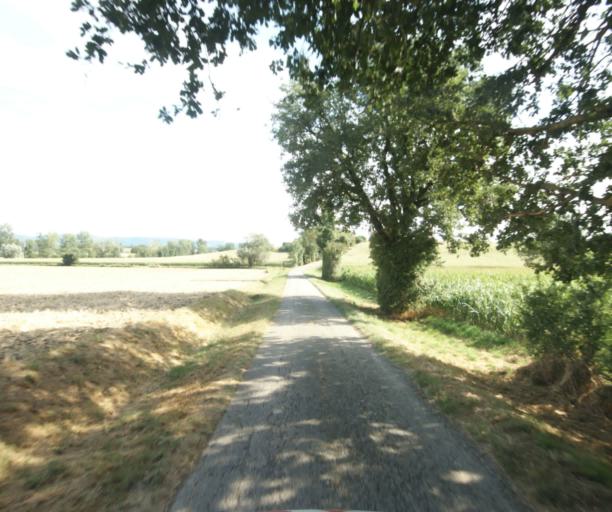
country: FR
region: Midi-Pyrenees
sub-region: Departement du Tarn
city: Puylaurens
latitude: 43.5245
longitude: 1.9892
